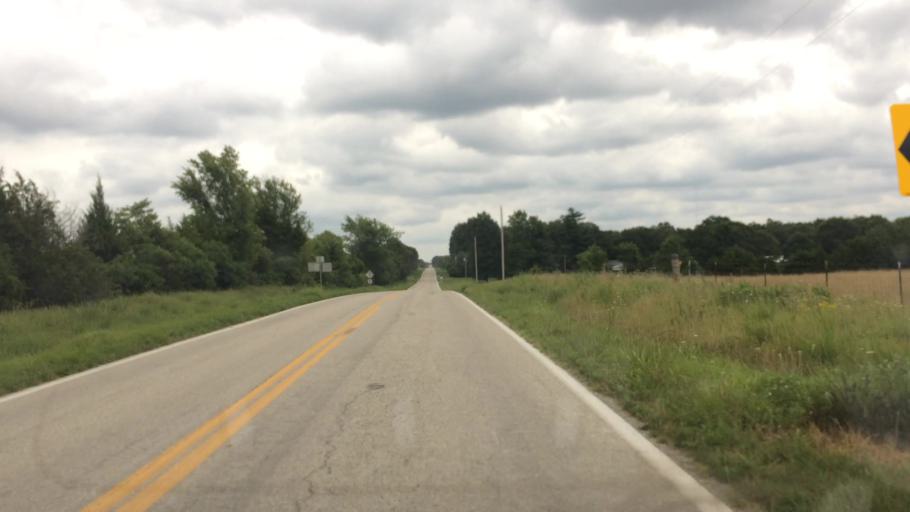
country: US
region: Missouri
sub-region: Greene County
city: Strafford
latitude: 37.3006
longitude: -93.1736
